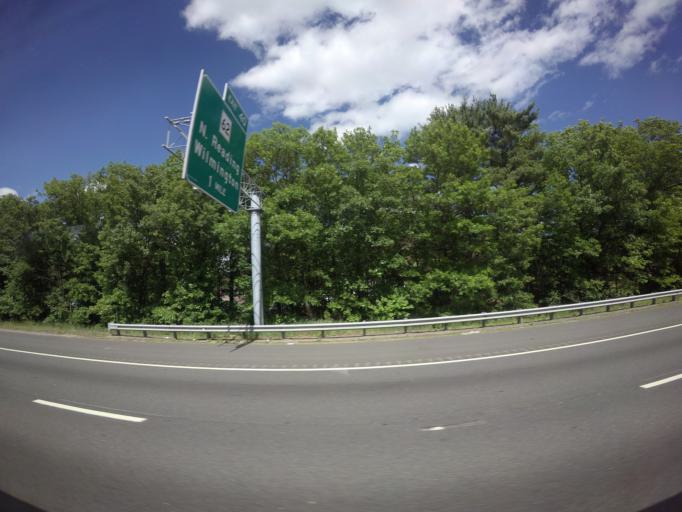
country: US
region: Massachusetts
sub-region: Middlesex County
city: Wilmington
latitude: 42.5614
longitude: -71.1422
